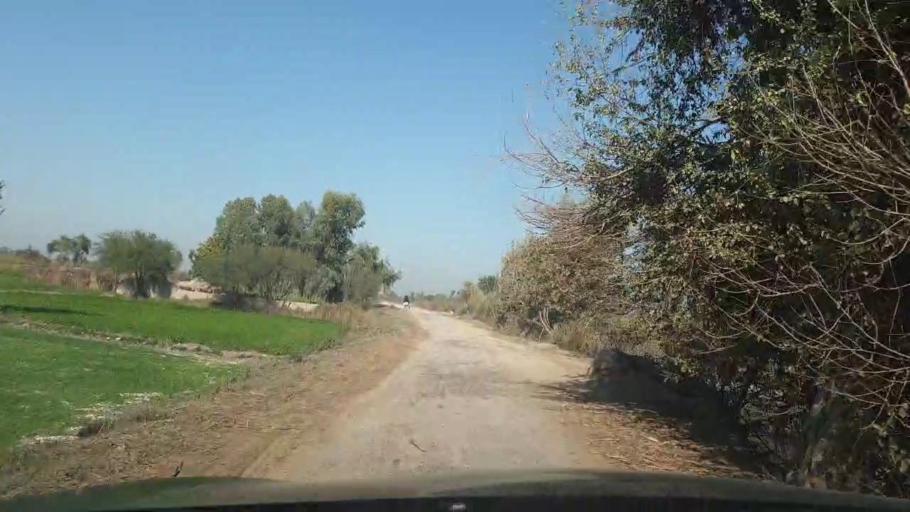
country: PK
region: Sindh
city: Ghotki
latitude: 27.9871
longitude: 69.4284
